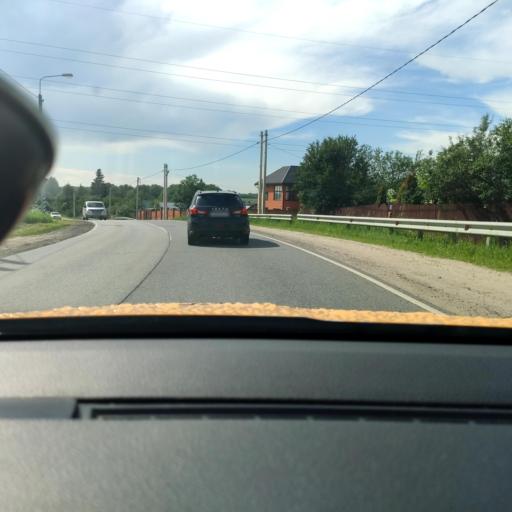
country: RU
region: Moskovskaya
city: Stupino
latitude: 54.9445
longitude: 38.0283
